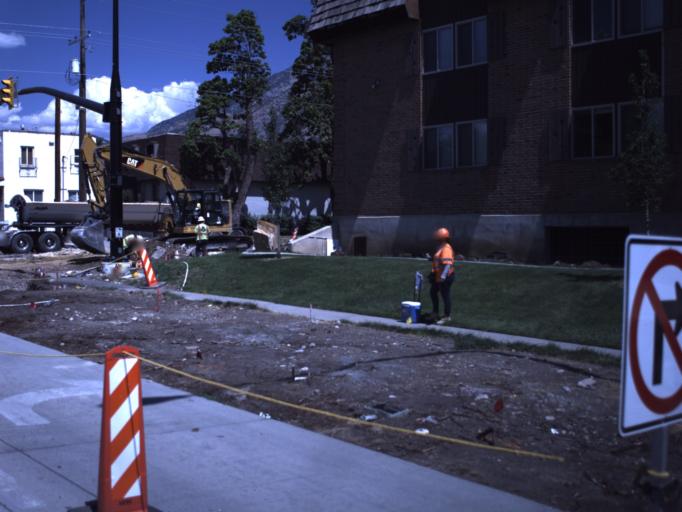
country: US
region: Utah
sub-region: Utah County
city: Provo
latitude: 40.2427
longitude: -111.6586
